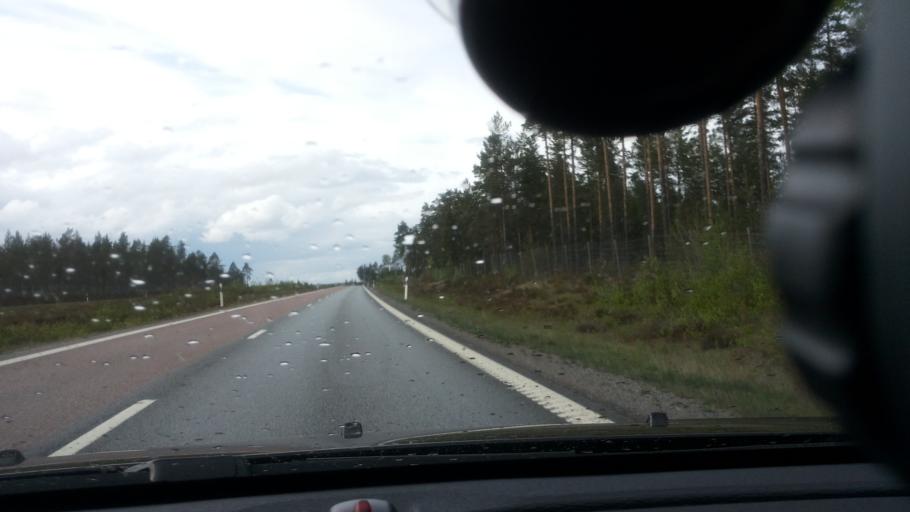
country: SE
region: Gaevleborg
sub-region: Soderhamns Kommun
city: Soderhamn
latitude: 61.3868
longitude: 16.9924
